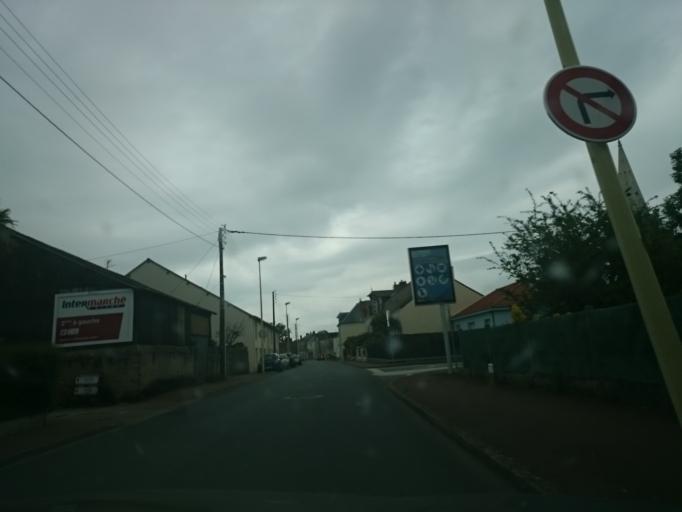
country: FR
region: Pays de la Loire
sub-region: Departement de la Loire-Atlantique
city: Le Pellerin
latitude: 47.1987
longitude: -1.7510
